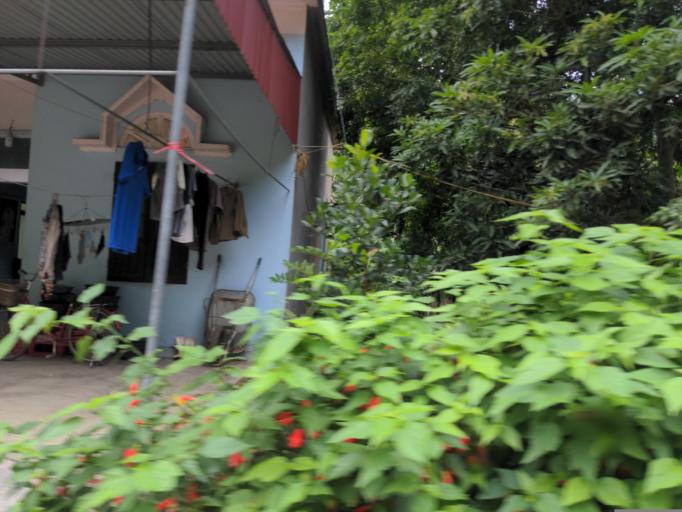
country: VN
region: Hai Phong
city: Cat Ba
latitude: 20.7986
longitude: 107.0427
